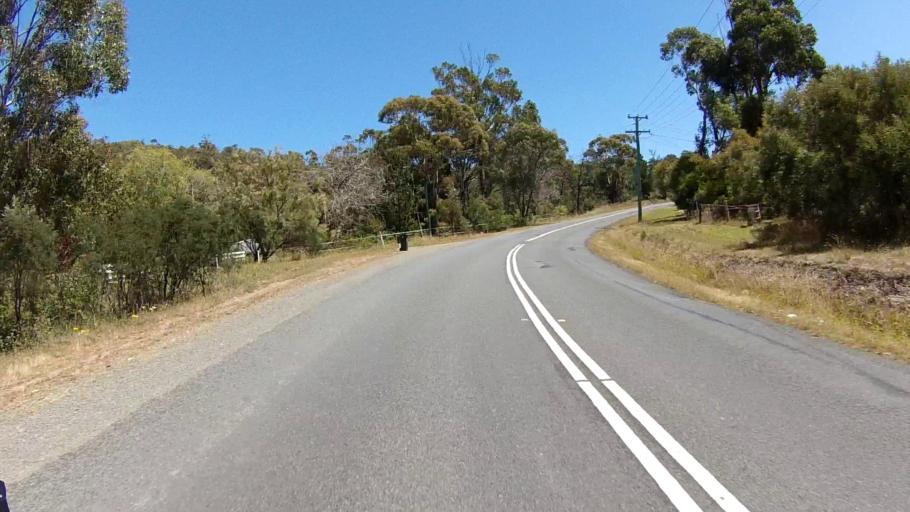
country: AU
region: Tasmania
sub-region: Clarence
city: Howrah
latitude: -42.8649
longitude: 147.4207
